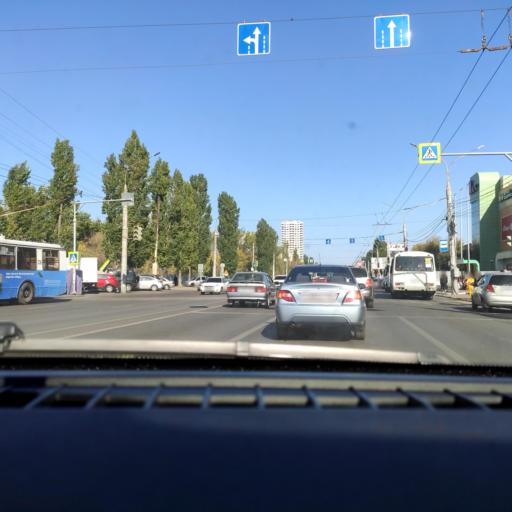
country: RU
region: Voronezj
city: Voronezh
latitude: 51.6970
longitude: 39.2717
